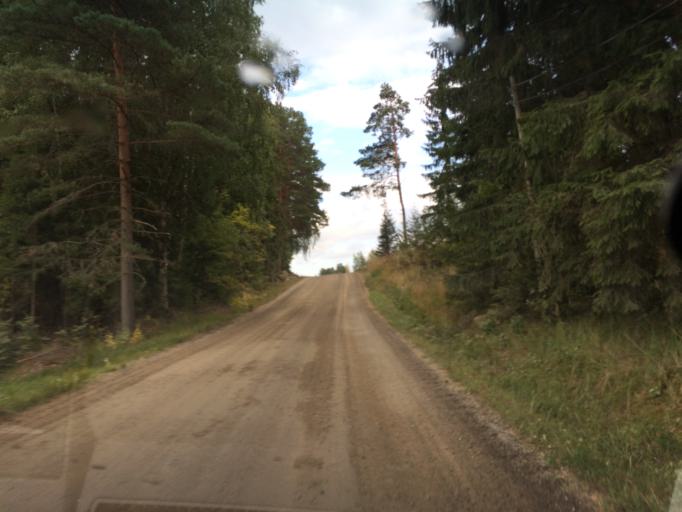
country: FI
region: Pirkanmaa
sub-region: Tampere
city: Luopioinen
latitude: 61.2617
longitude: 24.7034
